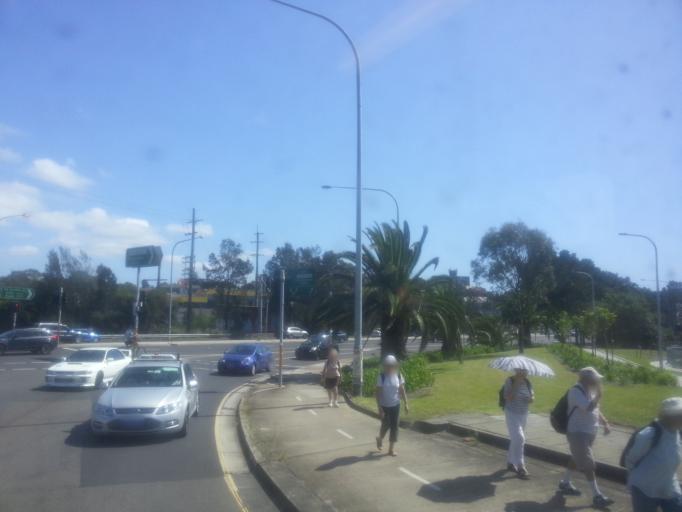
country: AU
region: New South Wales
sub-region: Leichhardt
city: Lilyfield
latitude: -33.8713
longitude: 151.1732
